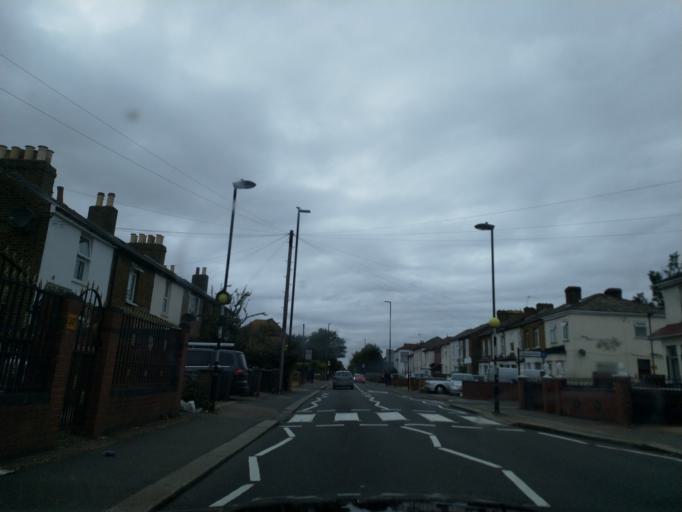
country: GB
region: England
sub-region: Greater London
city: Hounslow
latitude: 51.4615
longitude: -0.3756
